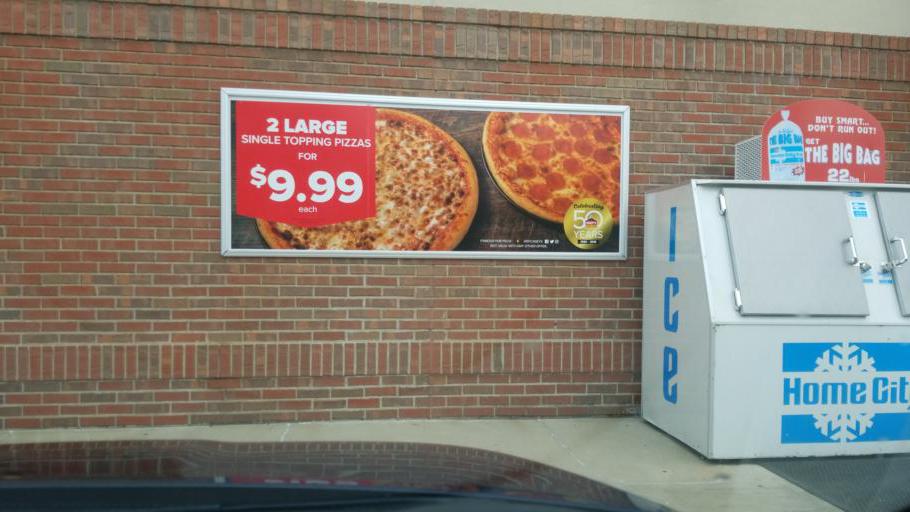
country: US
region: Tennessee
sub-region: Humphreys County
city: Waverly
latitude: 36.0845
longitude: -87.8039
